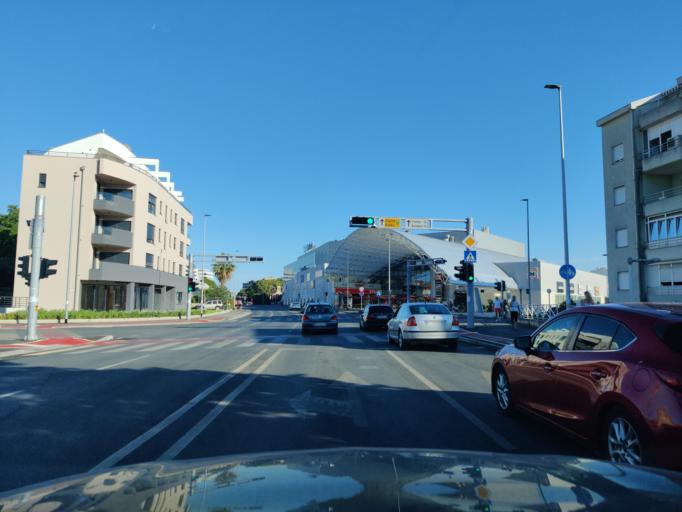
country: HR
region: Zadarska
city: Zadar
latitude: 44.1118
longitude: 15.2373
